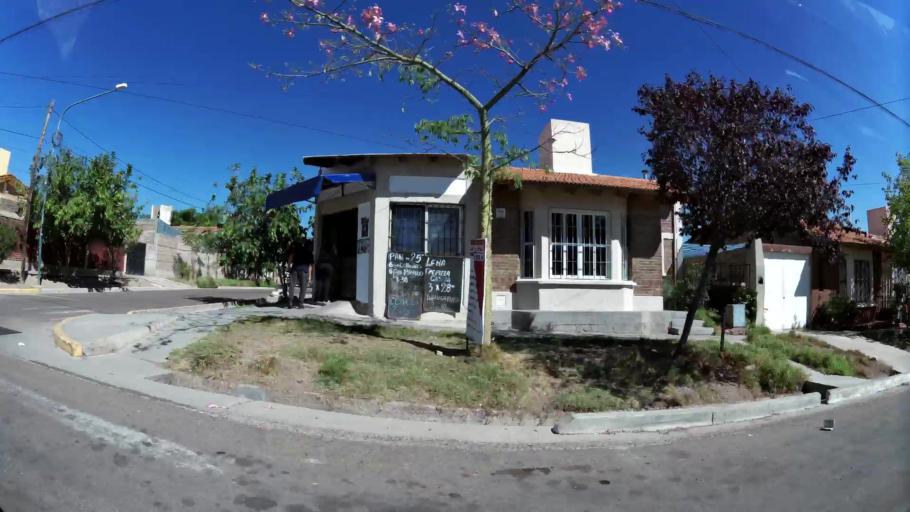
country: AR
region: Mendoza
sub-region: Departamento de Godoy Cruz
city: Godoy Cruz
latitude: -32.9104
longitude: -68.8792
